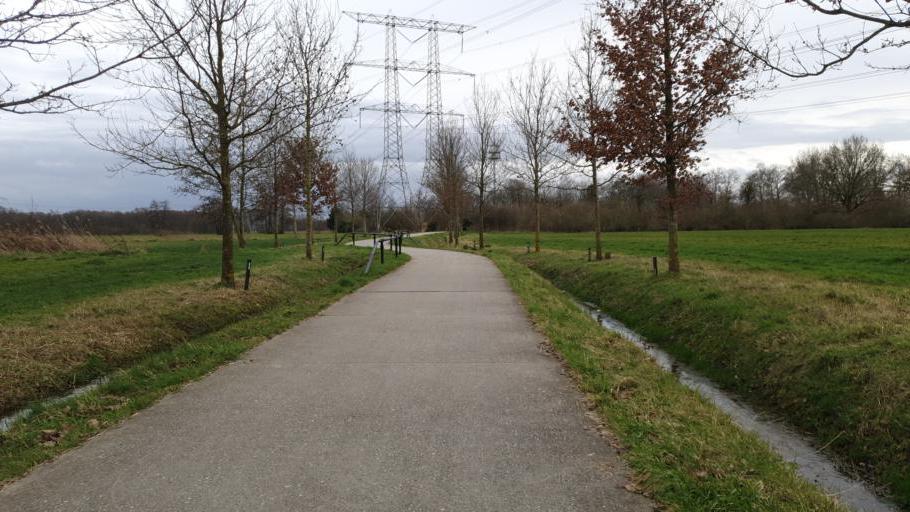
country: NL
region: North Brabant
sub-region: Gemeente Eindhoven
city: Tongelre
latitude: 51.4531
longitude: 5.5293
